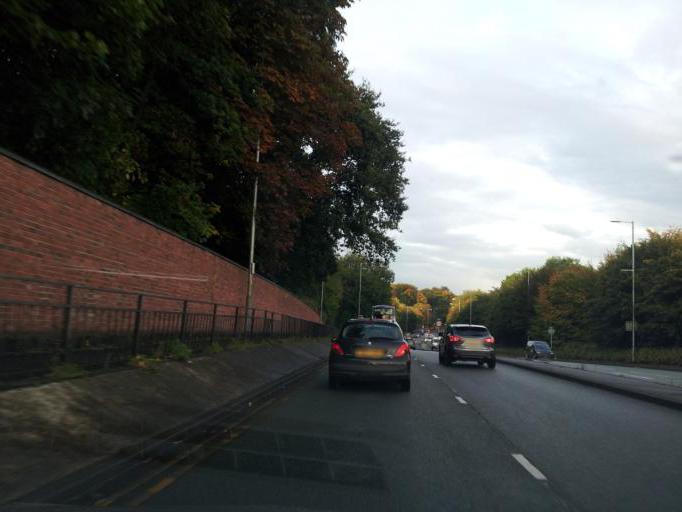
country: GB
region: England
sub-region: Manchester
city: Crumpsall
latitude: 53.5336
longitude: -2.2445
